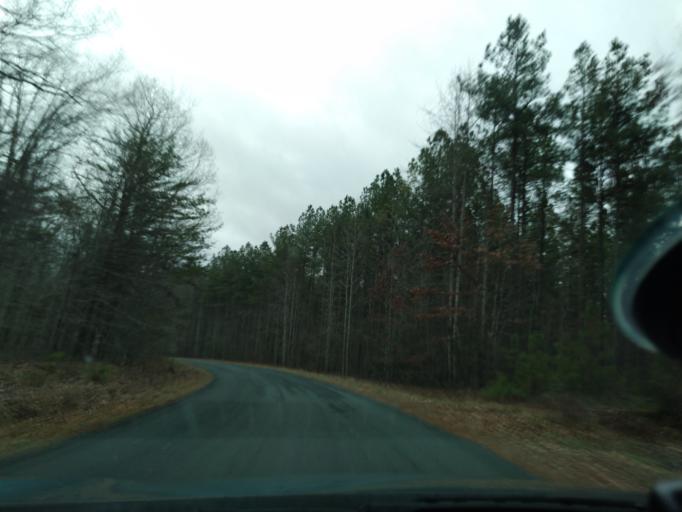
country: US
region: Virginia
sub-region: Appomattox County
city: Appomattox
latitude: 37.4006
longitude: -78.6651
